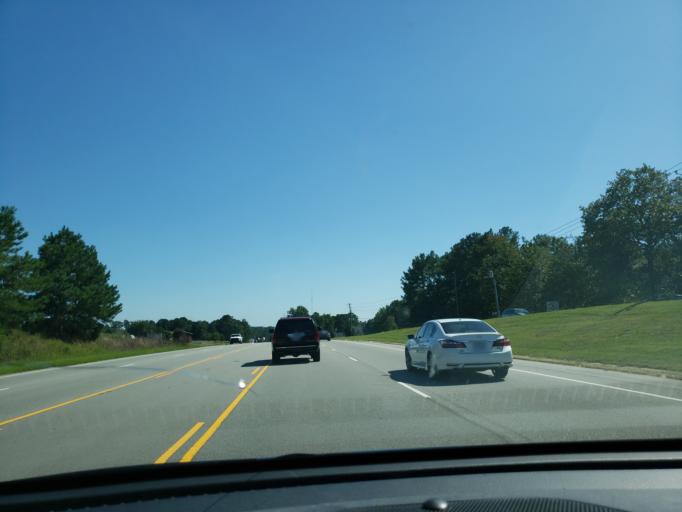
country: US
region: North Carolina
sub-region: Lee County
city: Broadway
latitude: 35.3664
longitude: -79.1112
